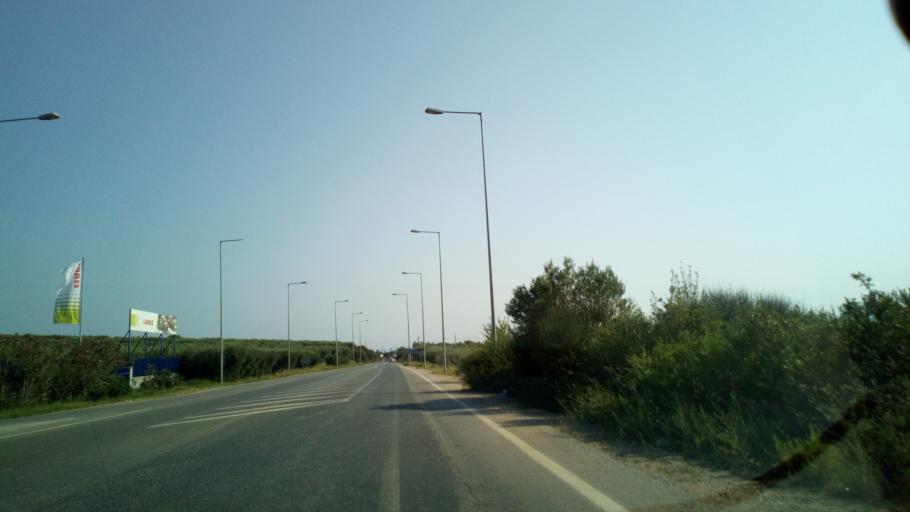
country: GR
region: Central Macedonia
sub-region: Nomos Chalkidikis
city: Kalyves Polygyrou
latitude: 40.2842
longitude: 23.4306
